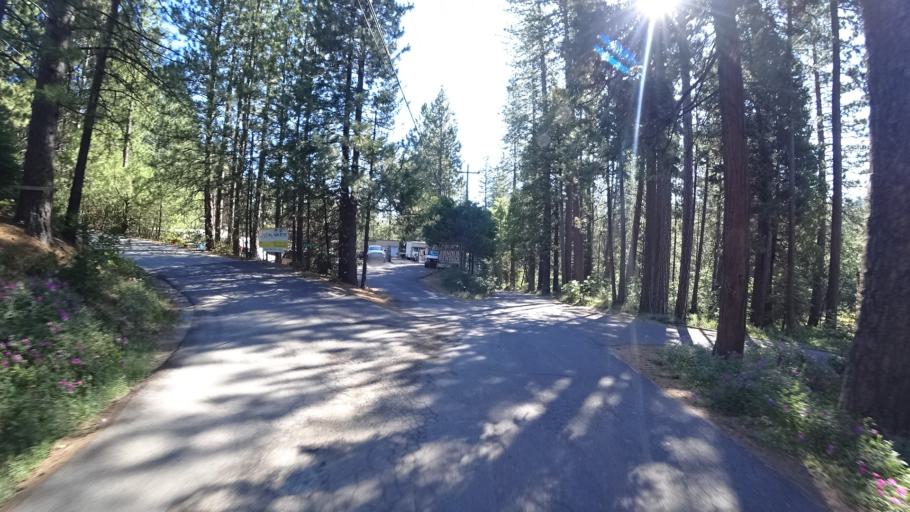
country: US
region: California
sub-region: Calaveras County
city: Arnold
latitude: 38.2593
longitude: -120.3474
